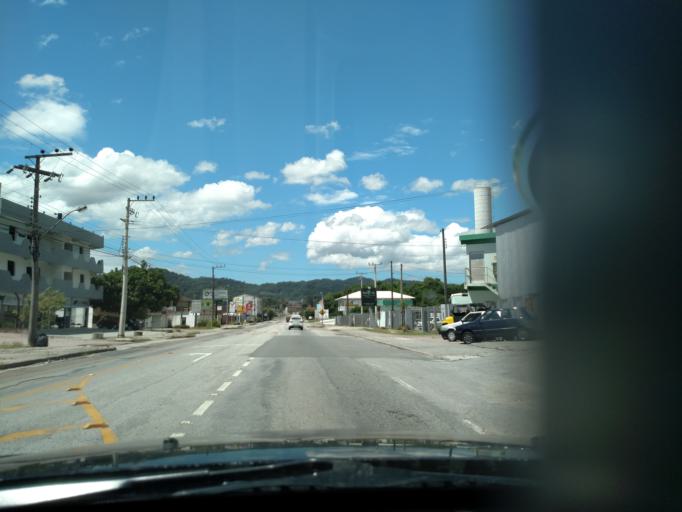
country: BR
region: Santa Catarina
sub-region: Gaspar
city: Gaspar
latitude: -26.8986
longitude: -49.0080
